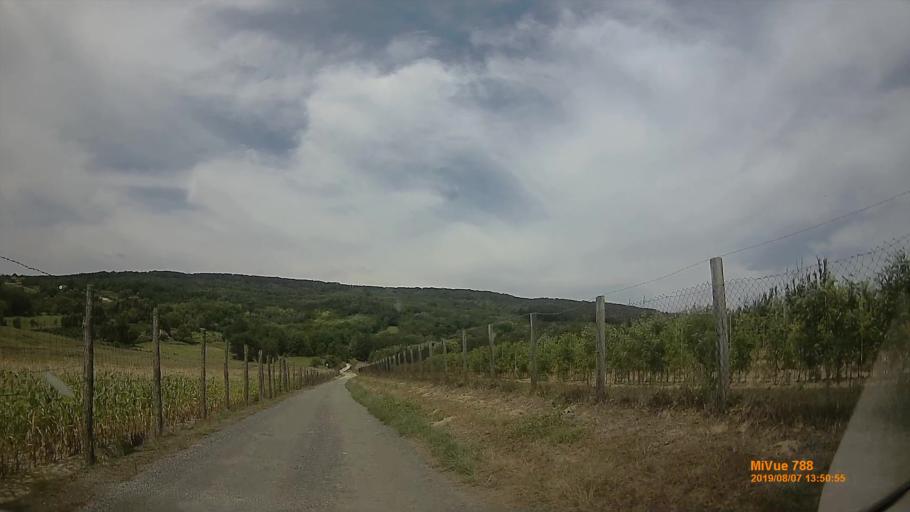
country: HU
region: Zala
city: Cserszegtomaj
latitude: 46.8913
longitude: 17.1872
